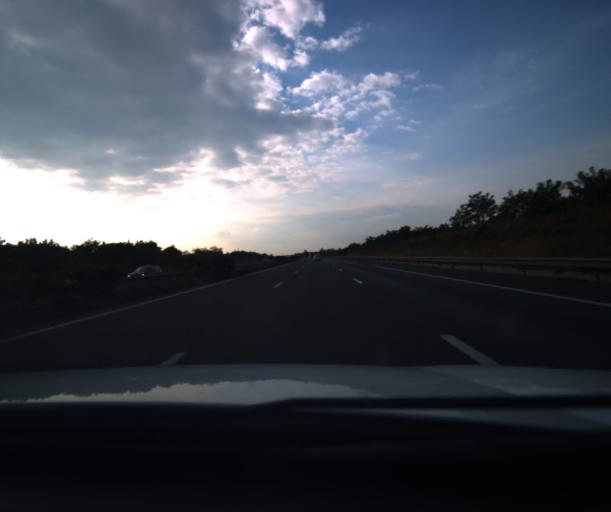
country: FR
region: Midi-Pyrenees
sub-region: Departement du Tarn-et-Garonne
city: Pompignan
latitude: 43.8341
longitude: 1.3389
